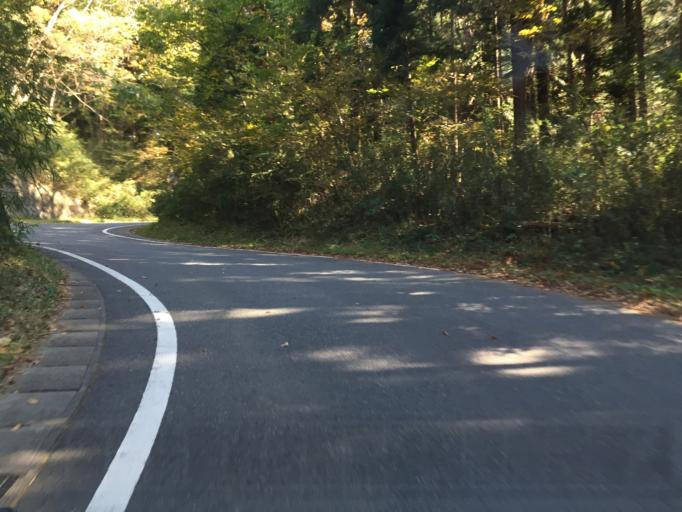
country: JP
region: Fukushima
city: Fukushima-shi
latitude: 37.7046
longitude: 140.4603
